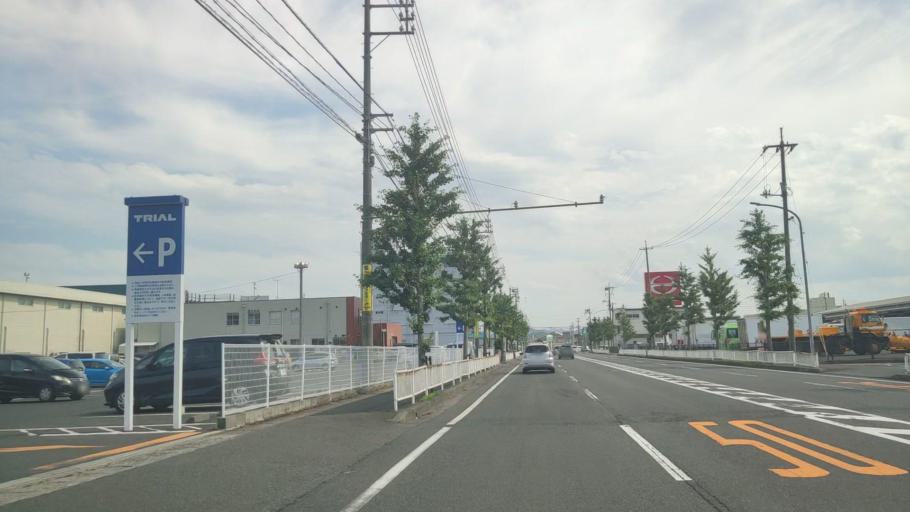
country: JP
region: Tottori
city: Tottori
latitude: 35.5164
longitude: 134.1921
